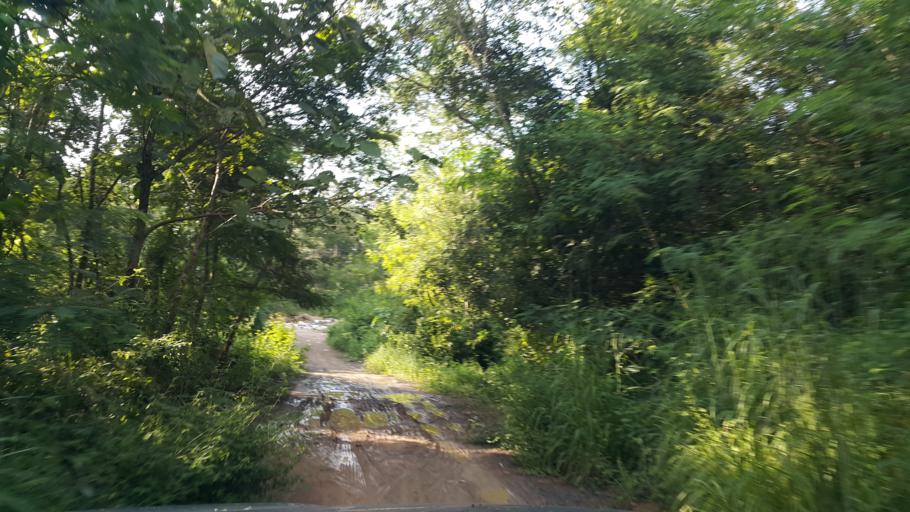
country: TH
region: Chiang Mai
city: Mae On
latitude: 18.7199
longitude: 99.2192
